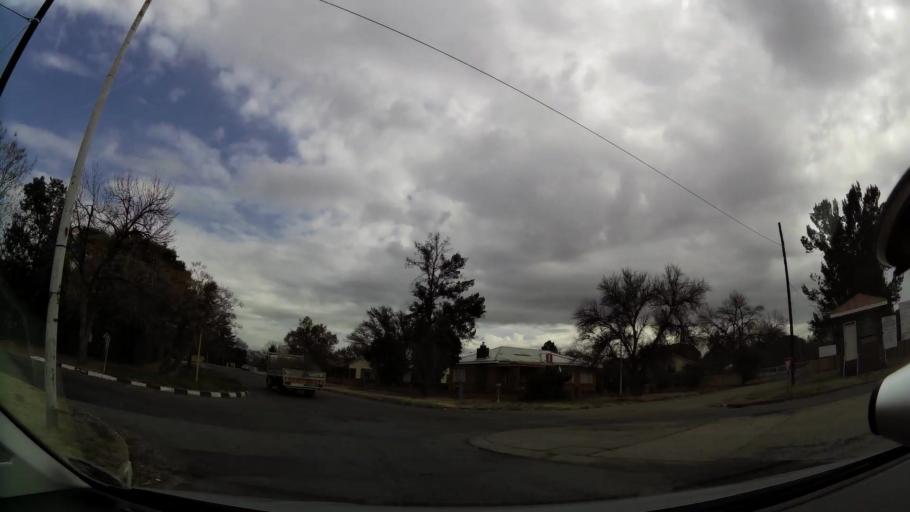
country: ZA
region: Orange Free State
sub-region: Fezile Dabi District Municipality
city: Kroonstad
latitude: -27.6323
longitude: 27.2330
